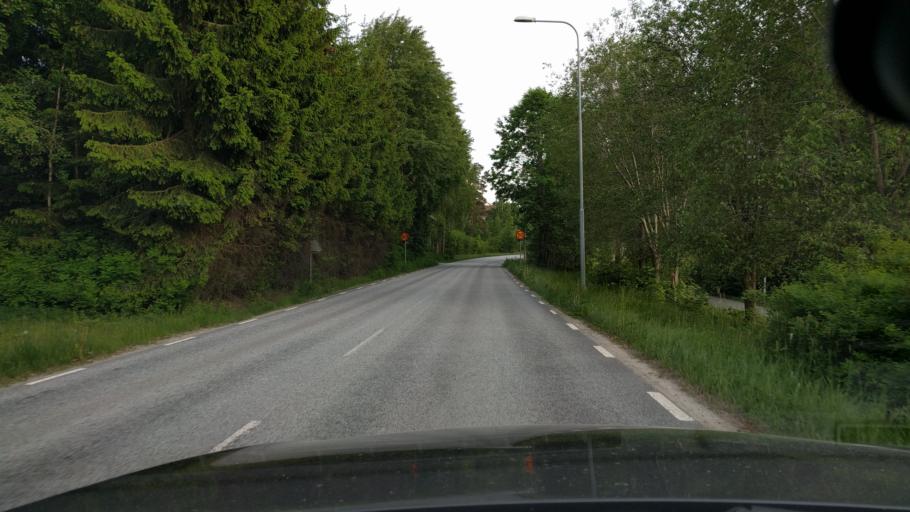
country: SE
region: Stockholm
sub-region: Vallentuna Kommun
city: Vallentuna
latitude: 59.5403
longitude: 18.0907
